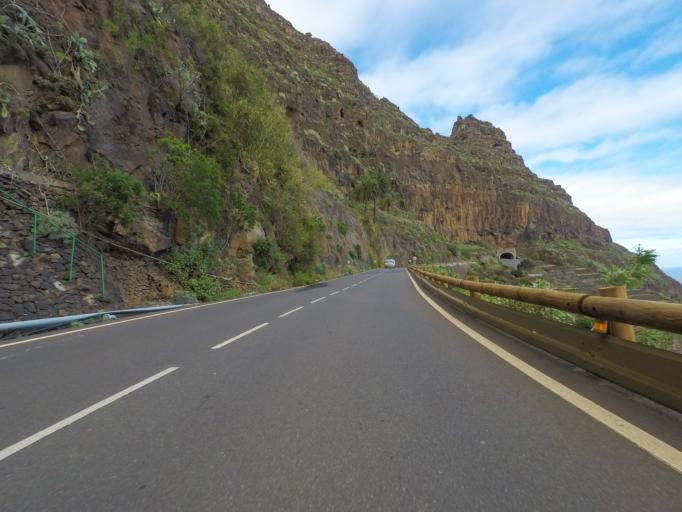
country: ES
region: Canary Islands
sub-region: Provincia de Santa Cruz de Tenerife
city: Agulo
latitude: 28.1889
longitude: -17.1982
